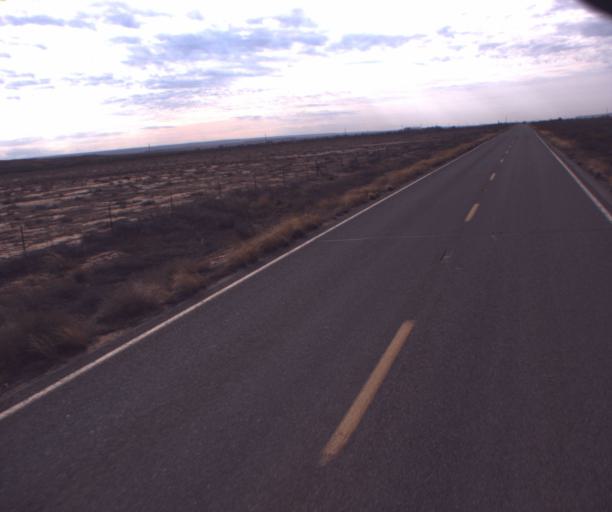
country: US
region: Arizona
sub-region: Apache County
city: Many Farms
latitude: 36.4510
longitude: -109.6079
